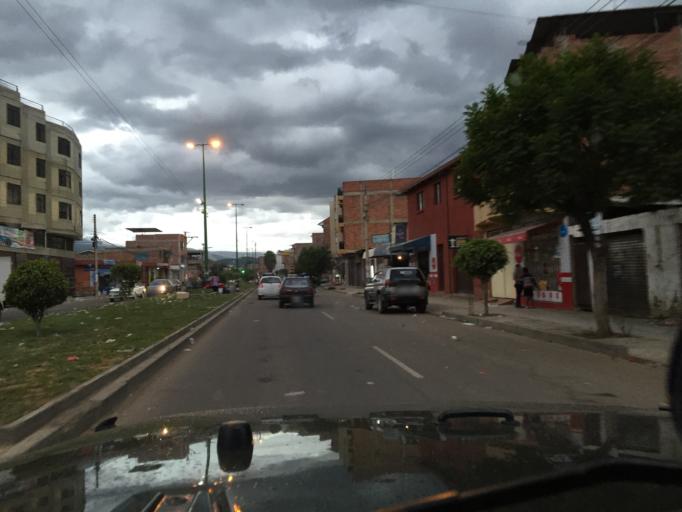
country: BO
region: Cochabamba
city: Cochabamba
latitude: -17.3968
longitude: -66.1912
